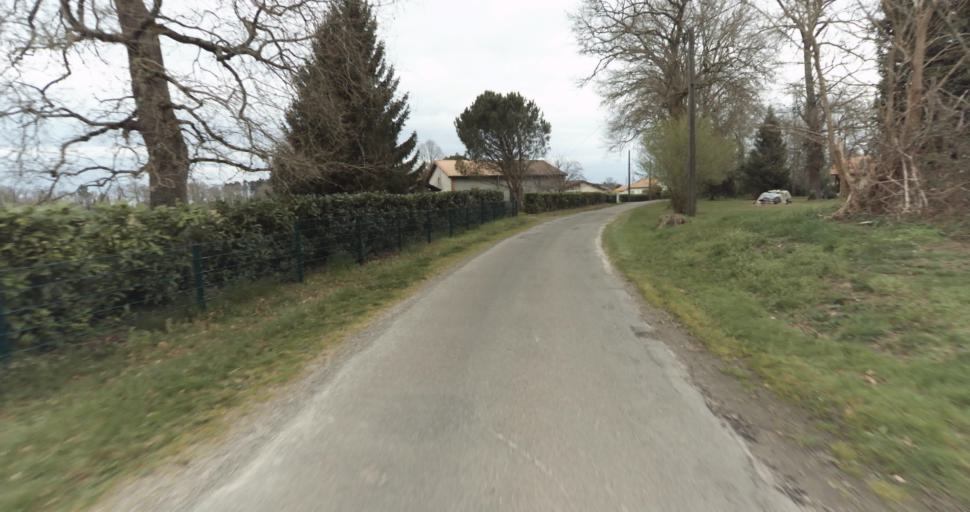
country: FR
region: Aquitaine
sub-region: Departement des Landes
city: Sarbazan
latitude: 44.0154
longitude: -0.3232
